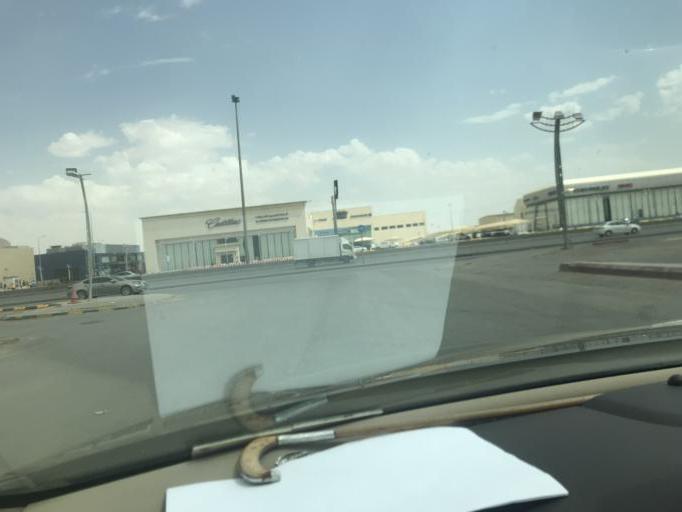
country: SA
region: Ar Riyad
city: Riyadh
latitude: 24.7281
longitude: 46.7824
